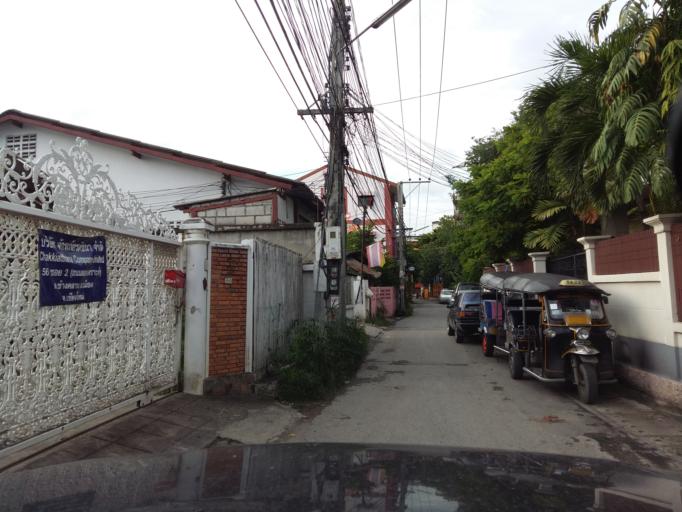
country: TH
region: Chiang Mai
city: Chiang Mai
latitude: 18.7814
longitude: 98.9948
